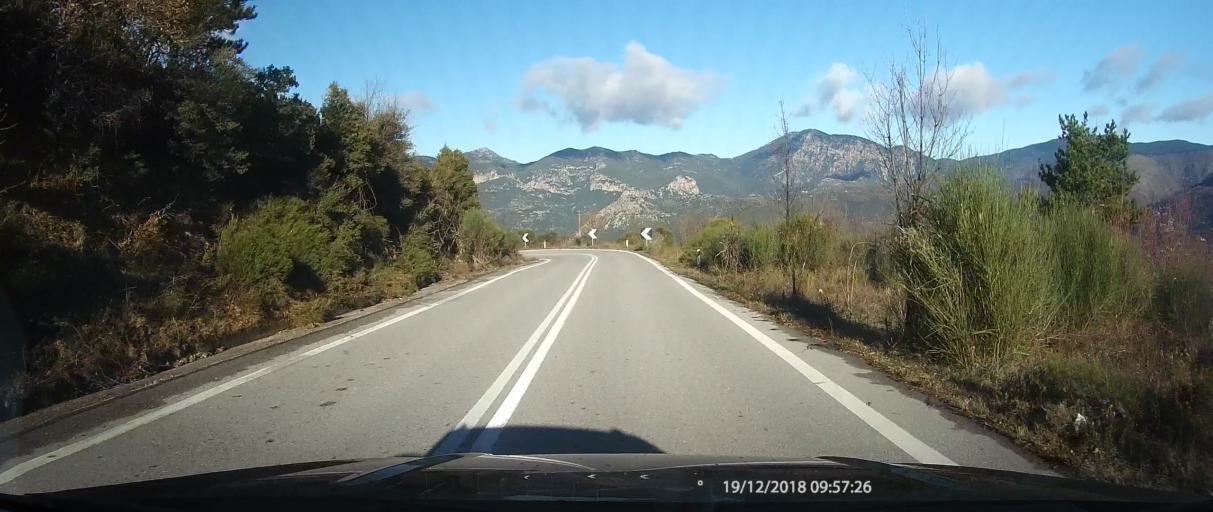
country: GR
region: Peloponnese
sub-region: Nomos Messinias
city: Paralia Vergas
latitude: 37.0892
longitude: 22.2383
